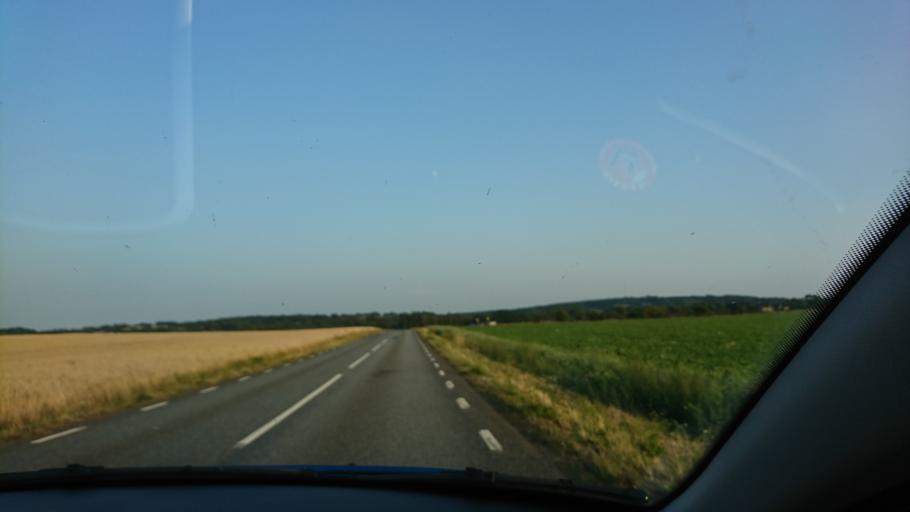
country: SE
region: Skane
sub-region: Simrishamns Kommun
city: Kivik
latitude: 55.6954
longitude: 14.1555
